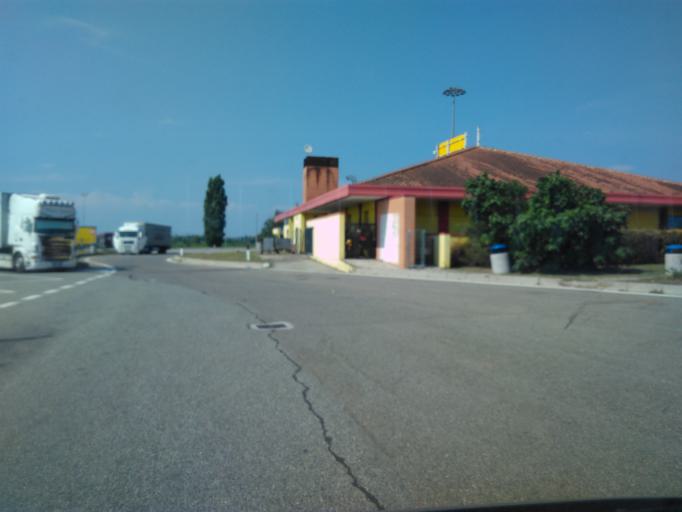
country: IT
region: Piedmont
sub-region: Provincia di Vercelli
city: Prarolo
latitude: 45.2860
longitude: 8.4701
